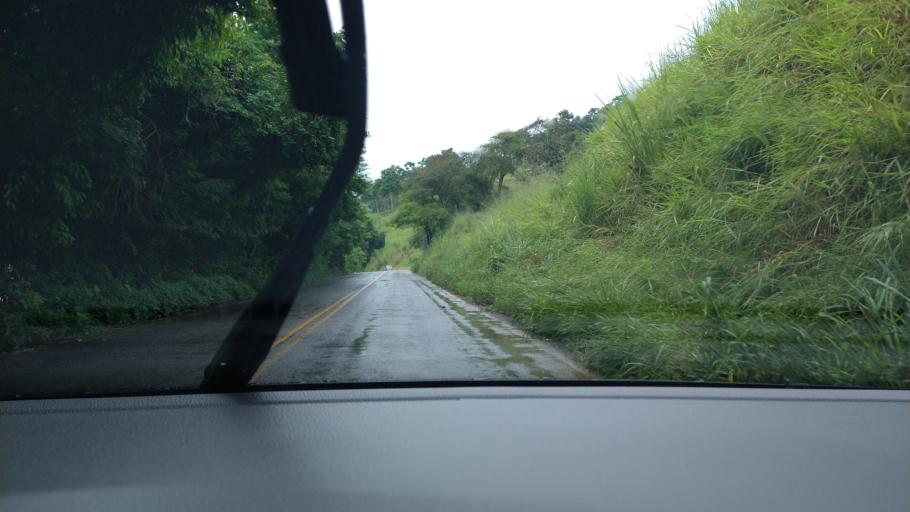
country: BR
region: Minas Gerais
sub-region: Ponte Nova
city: Ponte Nova
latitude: -20.3765
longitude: -42.8981
